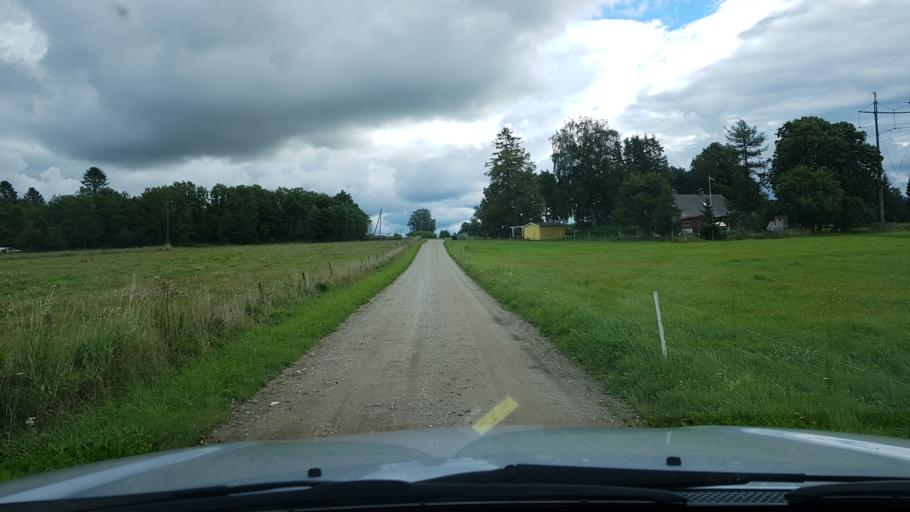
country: EE
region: Harju
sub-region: Raasiku vald
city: Arukula
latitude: 59.2689
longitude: 25.0606
